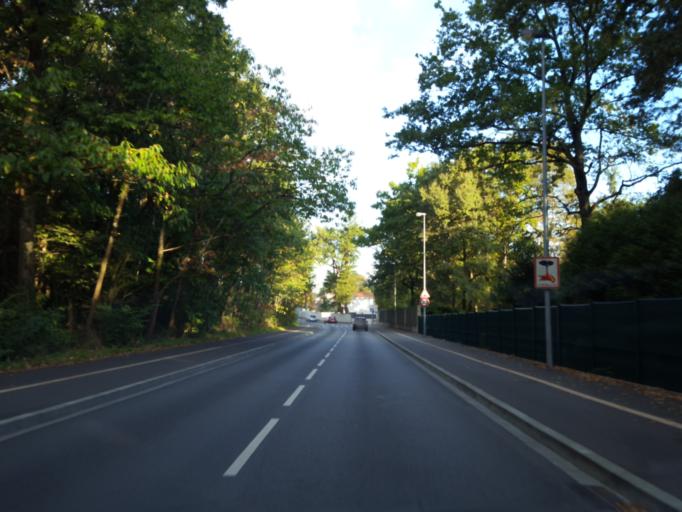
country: FR
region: Pays de la Loire
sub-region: Departement de la Loire-Atlantique
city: Basse-Goulaine
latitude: 47.1906
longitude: -1.4738
